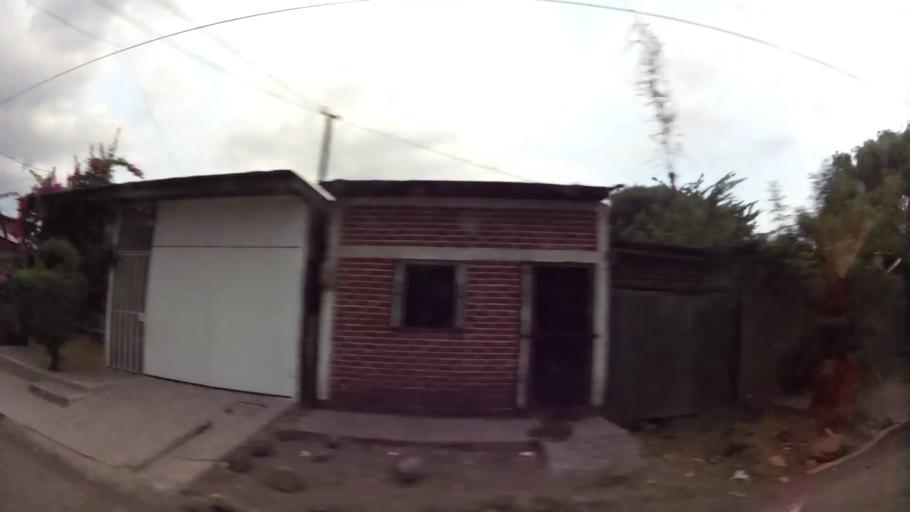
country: NI
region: Matagalpa
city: Ciudad Dario
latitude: 12.8547
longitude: -86.0956
